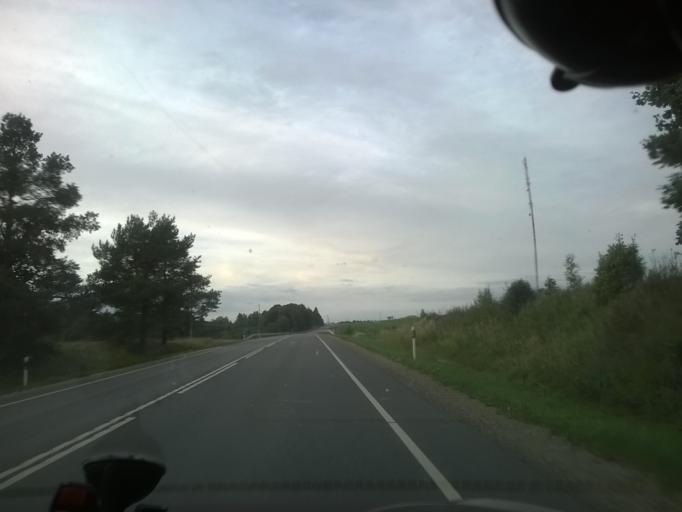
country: EE
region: Vorumaa
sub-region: Antsla vald
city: Vana-Antsla
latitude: 57.9824
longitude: 26.7722
